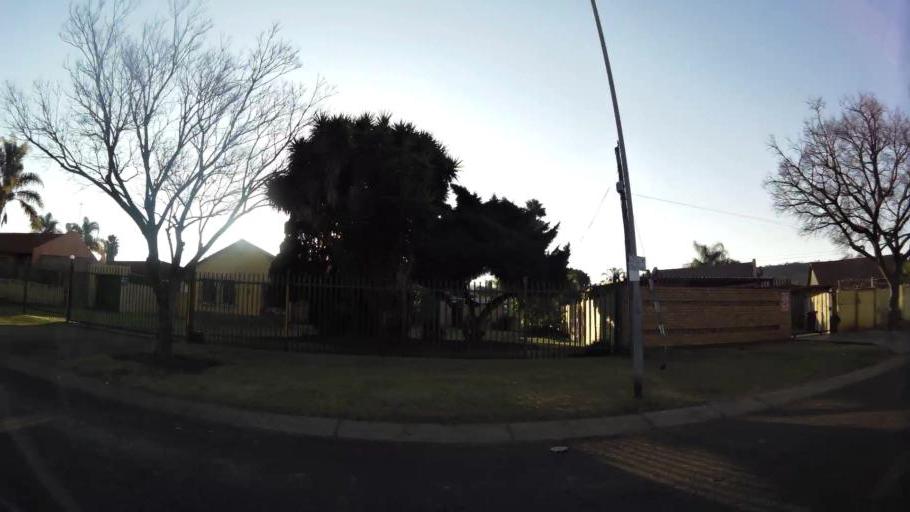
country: ZA
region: Gauteng
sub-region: City of Tshwane Metropolitan Municipality
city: Pretoria
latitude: -25.7381
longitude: 28.1090
